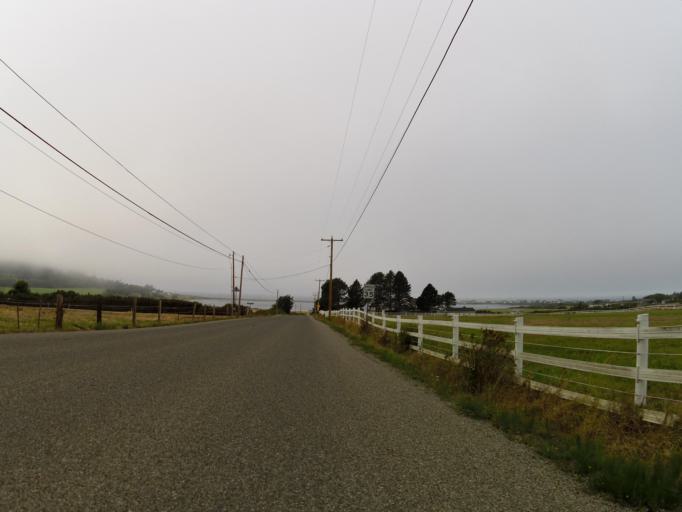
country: US
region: Washington
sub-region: Island County
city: Ault Field
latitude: 48.3007
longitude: -122.7078
